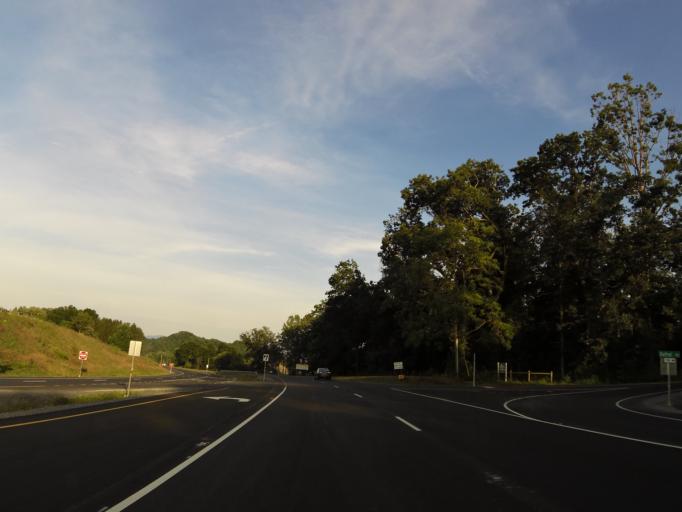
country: US
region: Virginia
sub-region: Washington County
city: Emory
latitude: 36.6814
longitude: -81.8795
